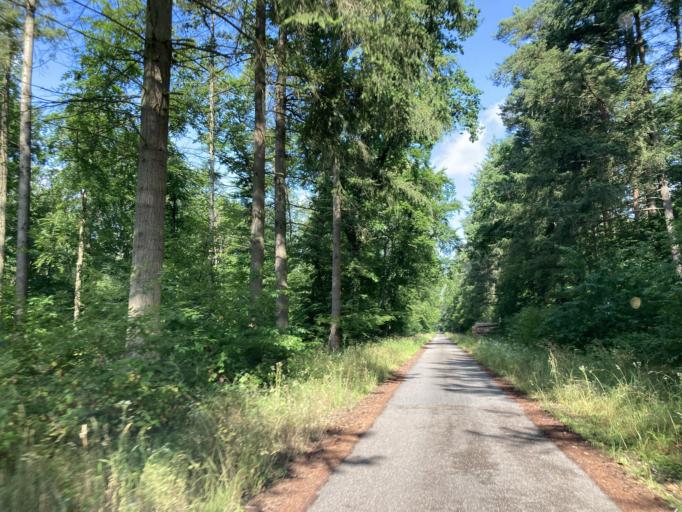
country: DE
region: Baden-Wuerttemberg
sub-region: Karlsruhe Region
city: Graben-Neudorf
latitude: 49.1602
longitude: 8.5164
